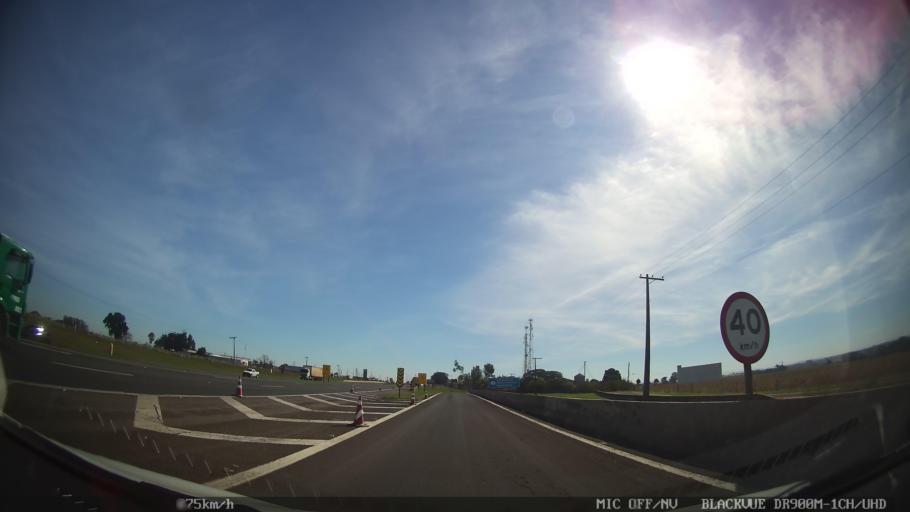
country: BR
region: Sao Paulo
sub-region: Pirassununga
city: Pirassununga
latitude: -22.0825
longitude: -47.4209
